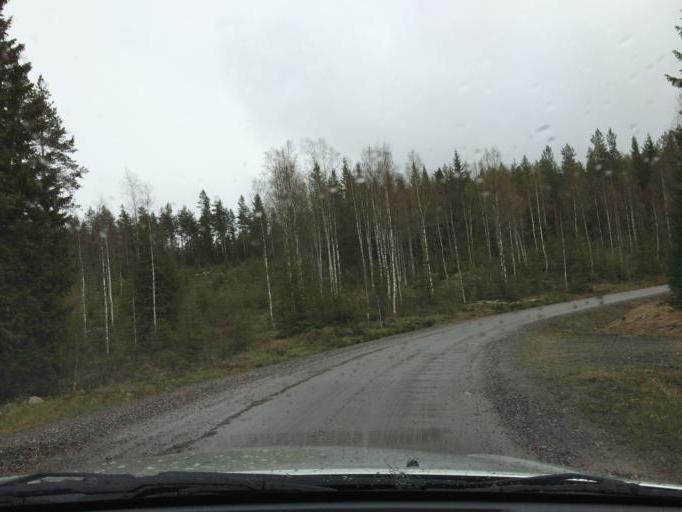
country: SE
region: Dalarna
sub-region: Ludvika Kommun
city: Abborrberget
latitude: 60.0401
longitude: 14.6395
